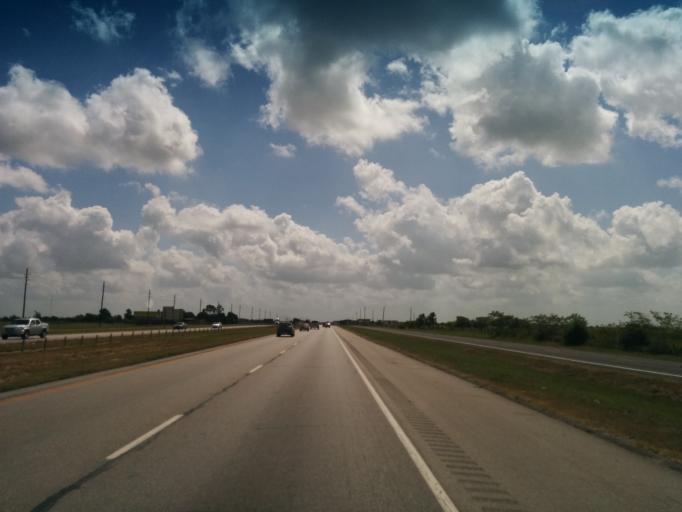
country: US
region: Texas
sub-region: Austin County
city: Sealy
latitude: 29.7545
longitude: -96.2518
